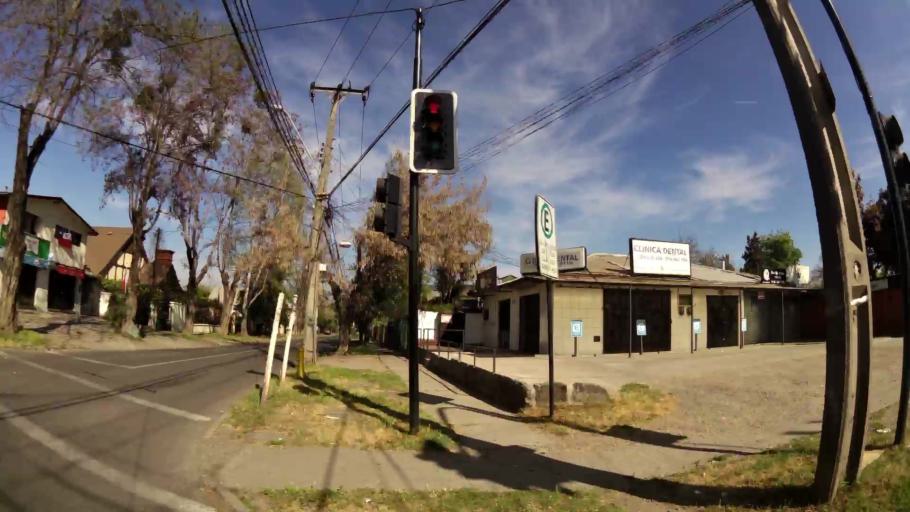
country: CL
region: Santiago Metropolitan
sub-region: Provincia de Santiago
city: Villa Presidente Frei, Nunoa, Santiago, Chile
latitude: -33.4462
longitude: -70.5515
